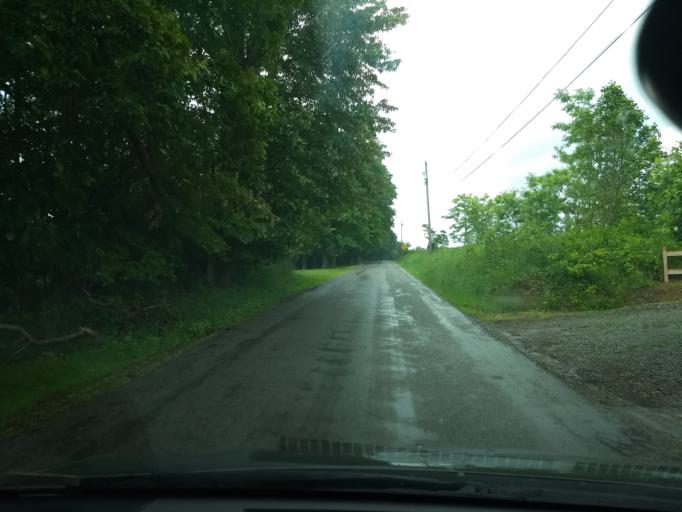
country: US
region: Pennsylvania
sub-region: Westmoreland County
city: Avonmore
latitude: 40.5403
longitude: -79.4939
